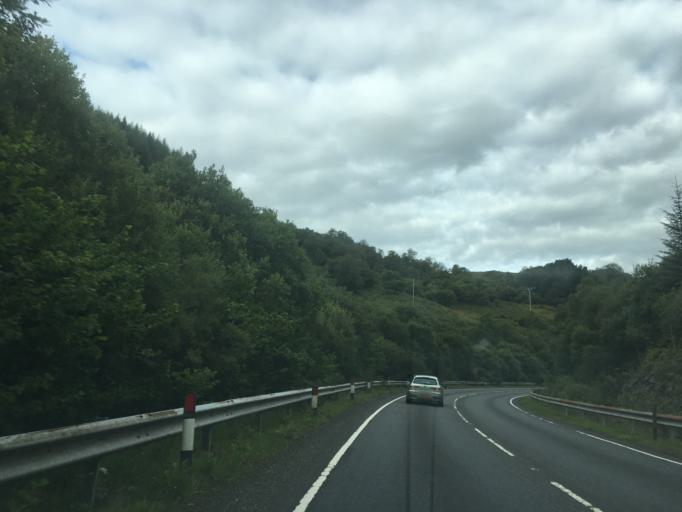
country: GB
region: Scotland
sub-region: Argyll and Bute
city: Oban
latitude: 56.3119
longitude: -5.4734
